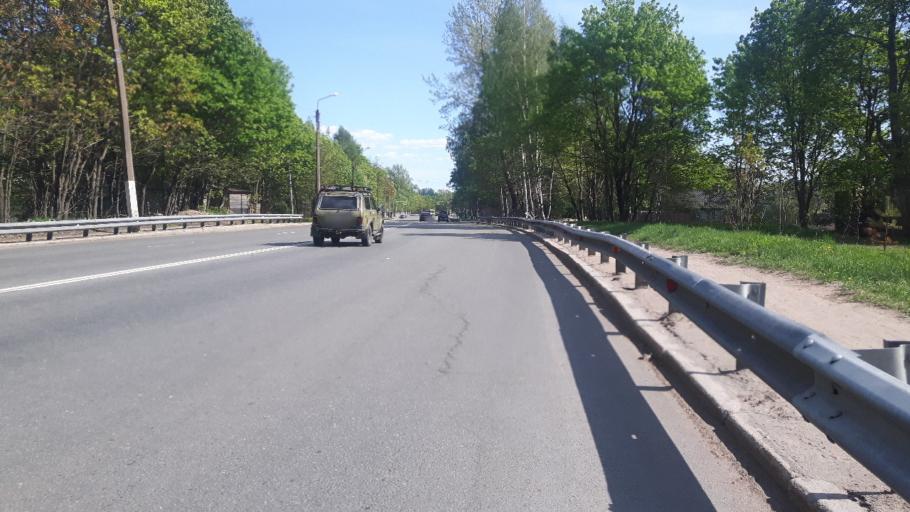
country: RU
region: Leningrad
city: Vyborg
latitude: 60.7297
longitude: 28.6996
